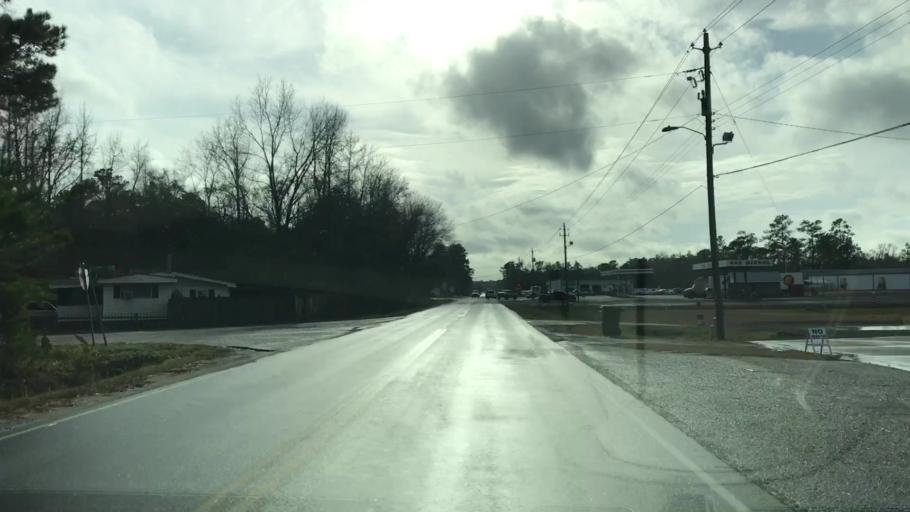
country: US
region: South Carolina
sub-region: Williamsburg County
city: Andrews
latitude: 33.4544
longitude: -79.5792
